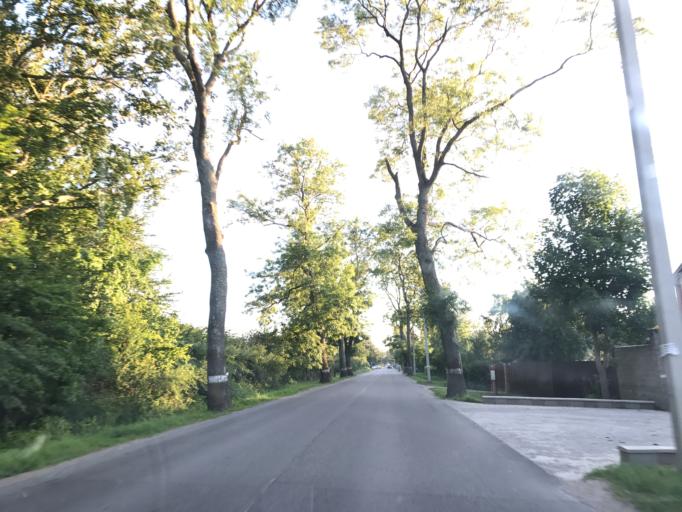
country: RU
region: Kaliningrad
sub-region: Zelenogradskiy Rayon
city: Zelenogradsk
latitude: 54.9400
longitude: 20.4546
